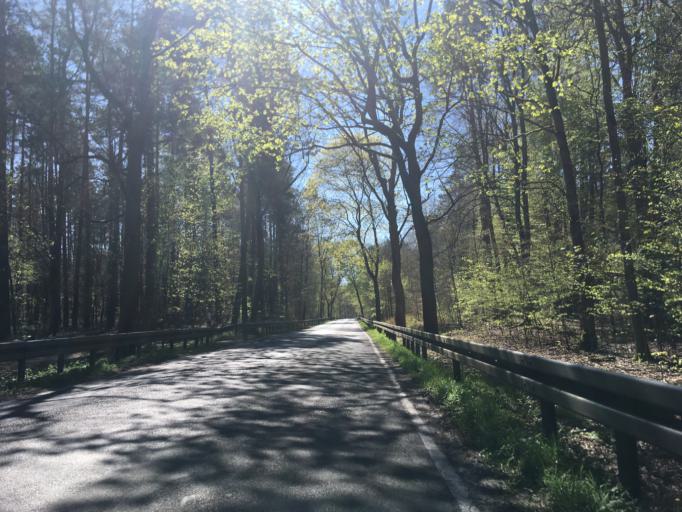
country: DE
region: Brandenburg
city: Bernau bei Berlin
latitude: 52.7194
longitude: 13.5717
